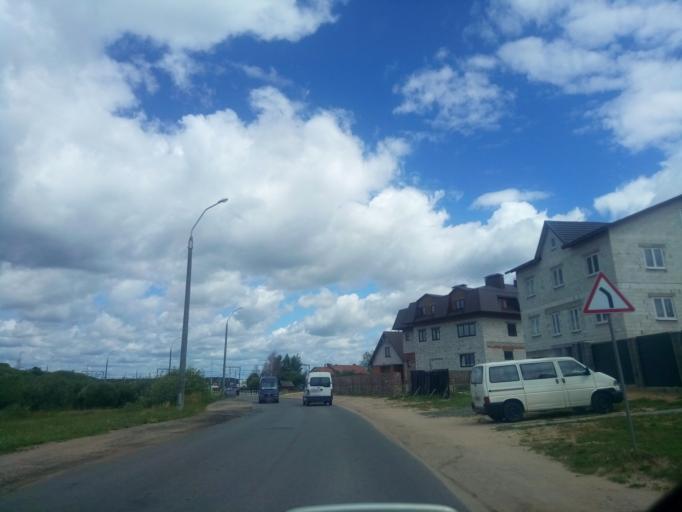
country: BY
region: Minsk
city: Zhdanovichy
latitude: 53.9387
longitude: 27.4354
